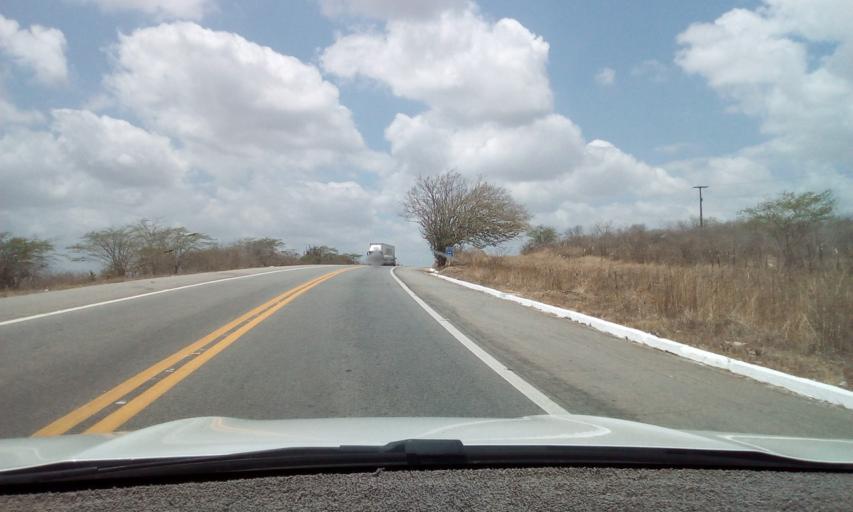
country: BR
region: Pernambuco
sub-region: Taquaritinga Do Norte
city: Taquaritinga do Norte
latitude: -7.7296
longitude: -36.0749
